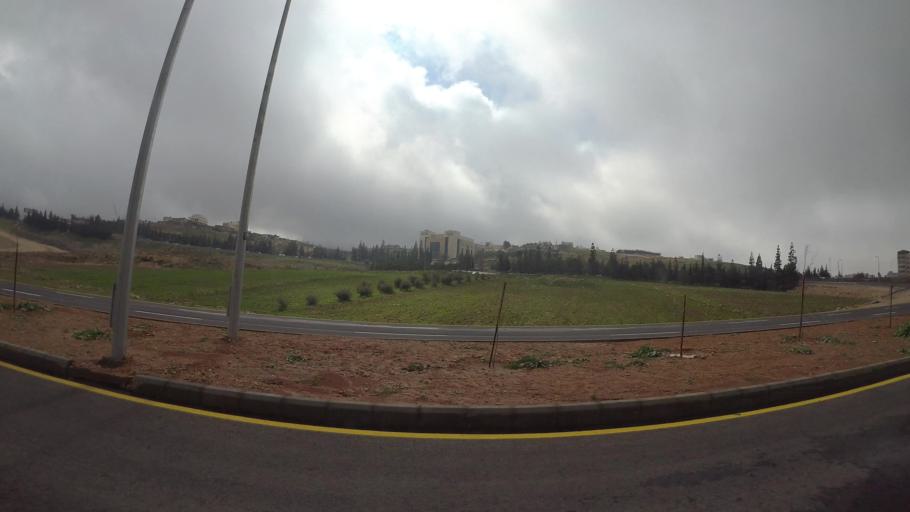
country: JO
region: Amman
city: Wadi as Sir
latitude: 31.9360
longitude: 35.8571
